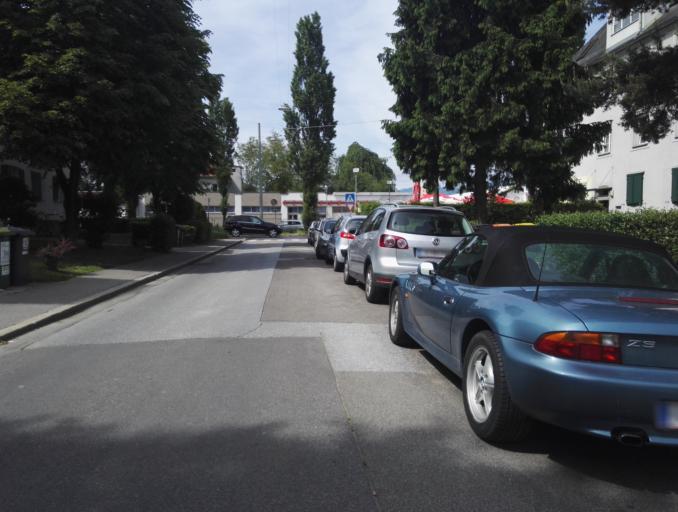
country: AT
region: Styria
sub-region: Graz Stadt
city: Wetzelsdorf
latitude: 47.0509
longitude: 15.4257
